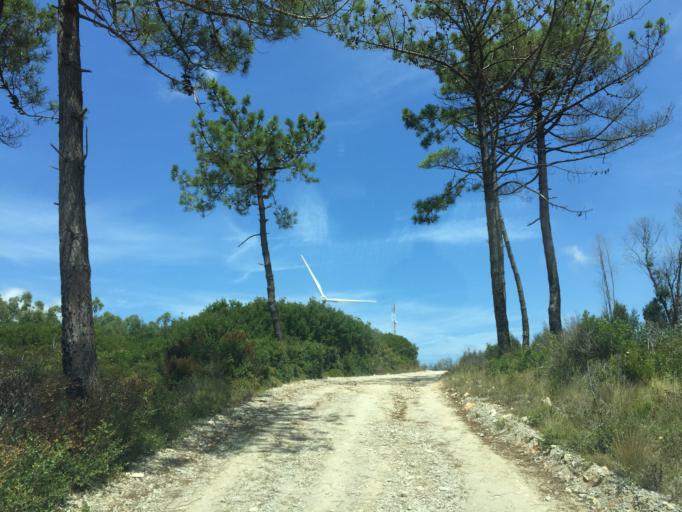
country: PT
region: Leiria
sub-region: Peniche
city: Atouguia da Baleia
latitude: 39.3194
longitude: -9.2609
